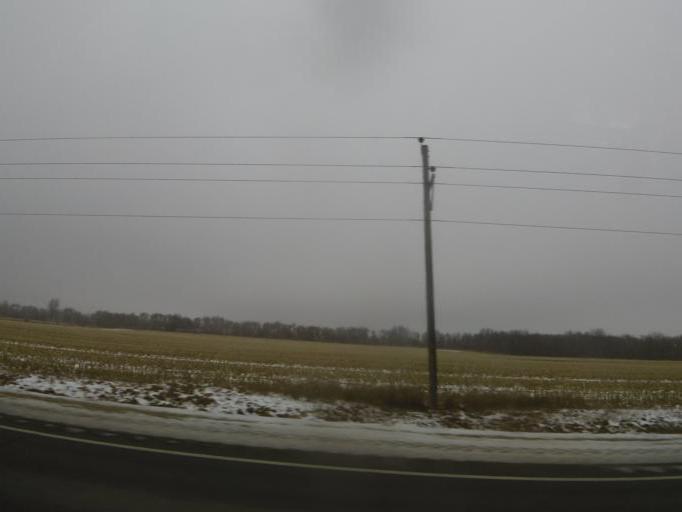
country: US
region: Minnesota
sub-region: Mower County
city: Grand Meadow
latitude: 43.7105
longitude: -92.5322
